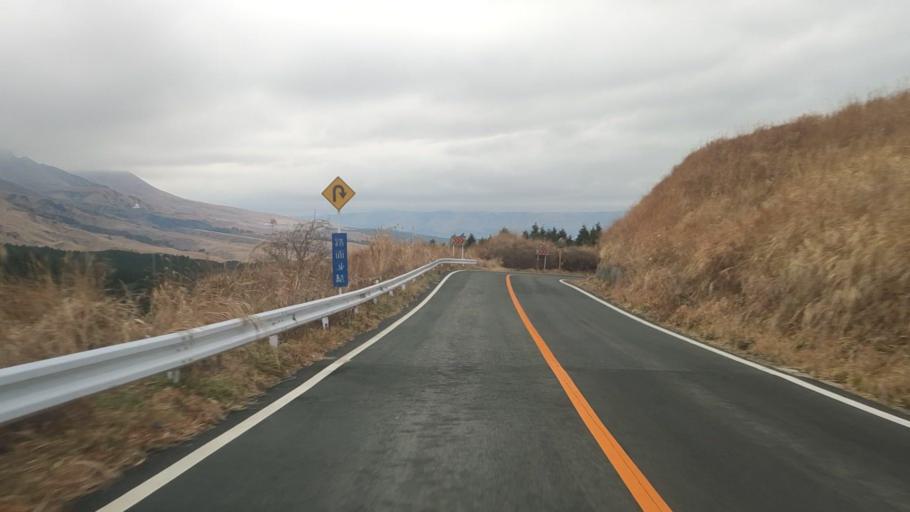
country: JP
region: Kumamoto
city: Aso
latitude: 32.9039
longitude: 131.1478
